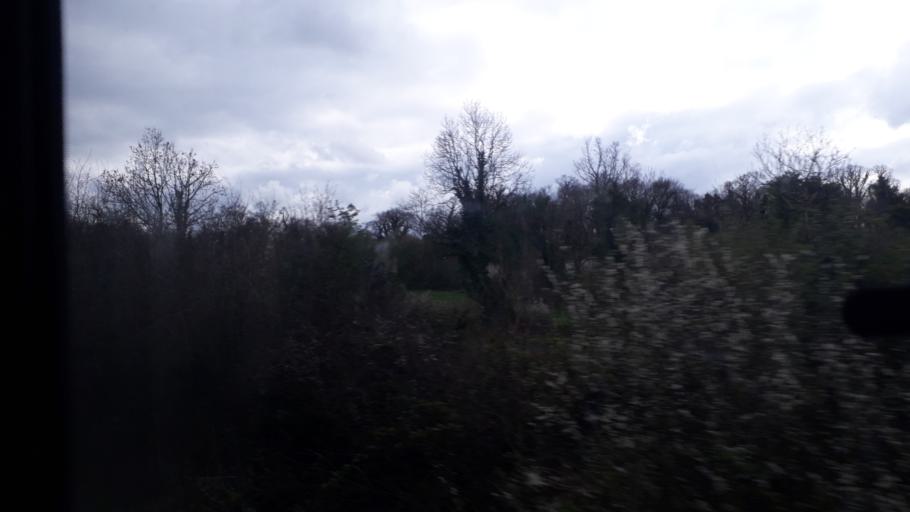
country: IE
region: Leinster
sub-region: An Longfort
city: Longford
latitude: 53.7851
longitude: -7.8379
